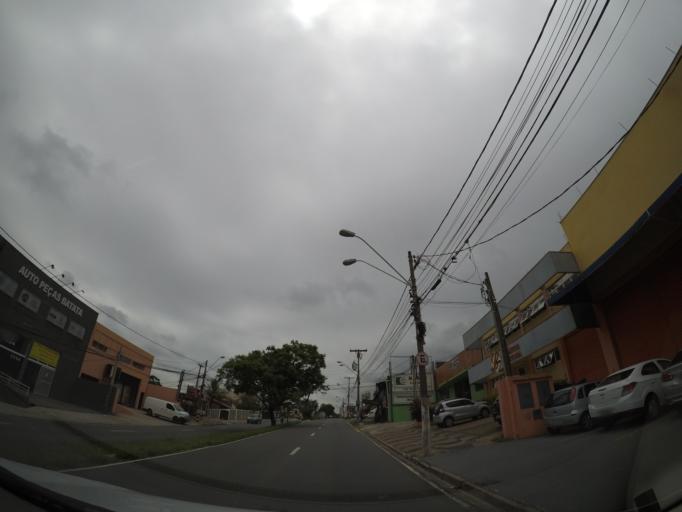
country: BR
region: Sao Paulo
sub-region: Campinas
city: Campinas
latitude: -22.9302
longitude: -47.0434
